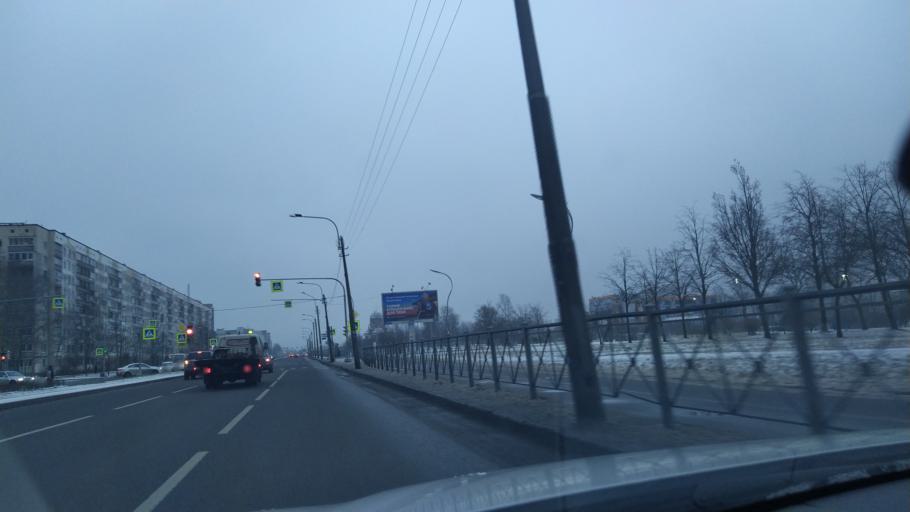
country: RU
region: St.-Petersburg
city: Grazhdanka
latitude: 60.0279
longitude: 30.4022
